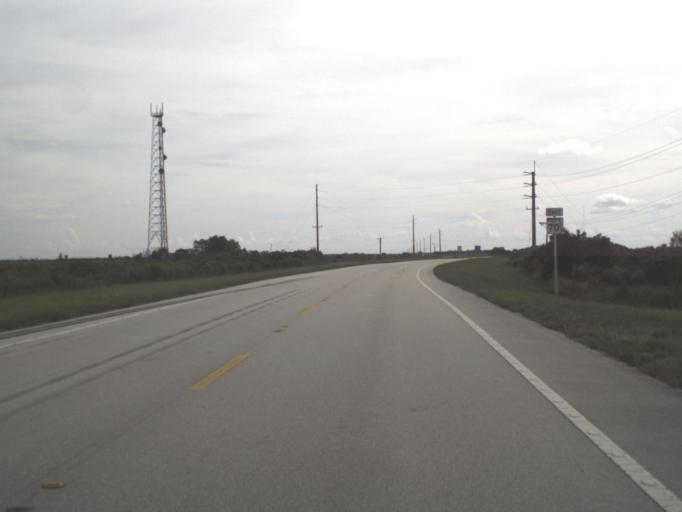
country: US
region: Florida
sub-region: Highlands County
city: Placid Lakes
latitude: 27.2096
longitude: -81.5625
